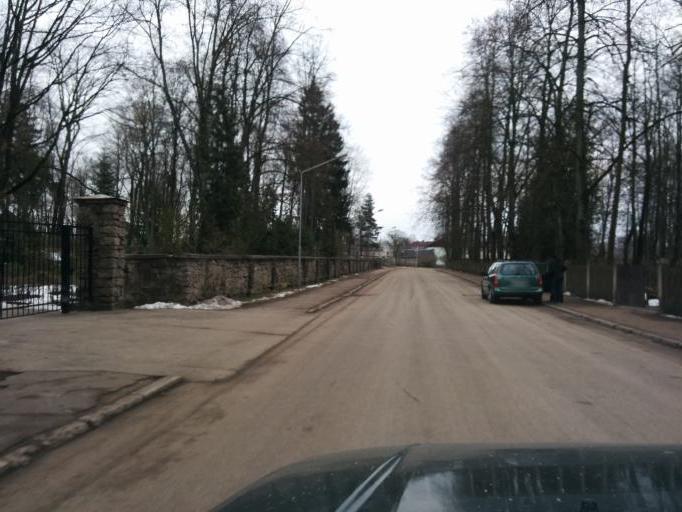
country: LV
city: Tireli
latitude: 56.9465
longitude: 23.6249
